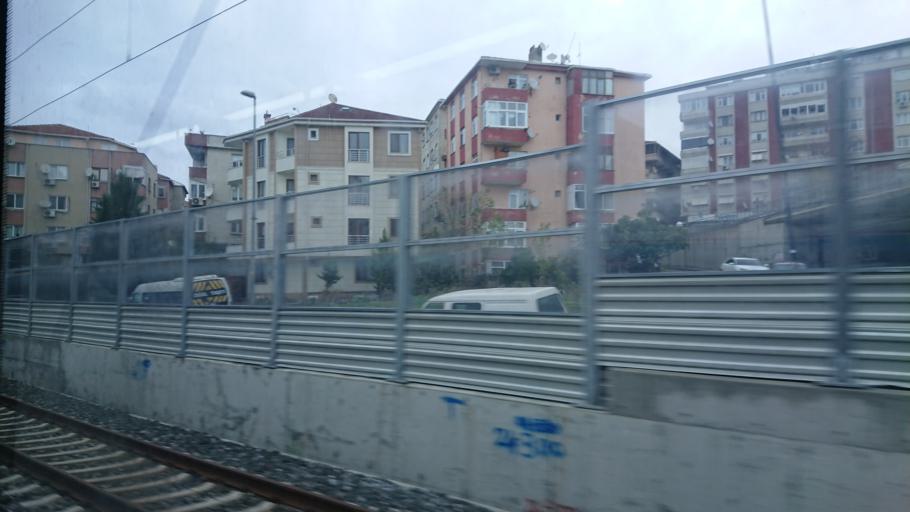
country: TR
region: Istanbul
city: Mahmutbey
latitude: 40.9941
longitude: 28.7690
